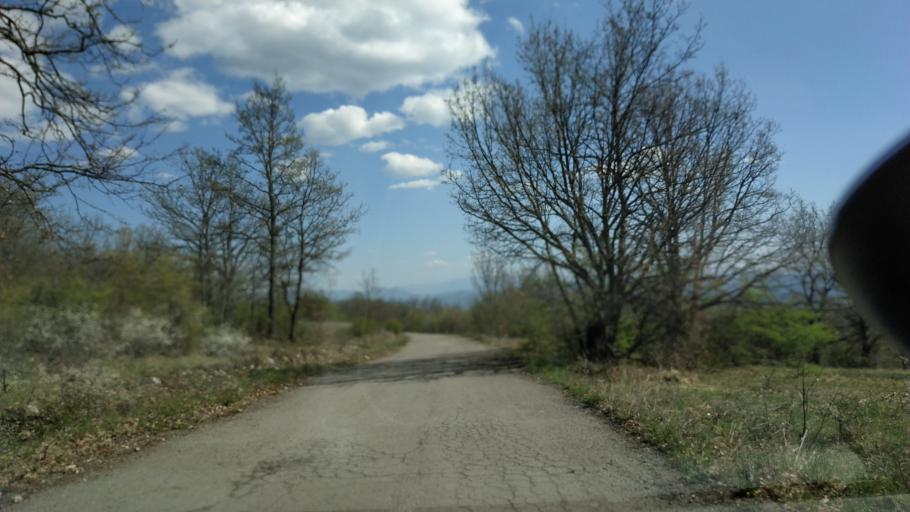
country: RS
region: Central Serbia
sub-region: Zajecarski Okrug
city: Soko Banja
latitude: 43.5544
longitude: 21.8936
